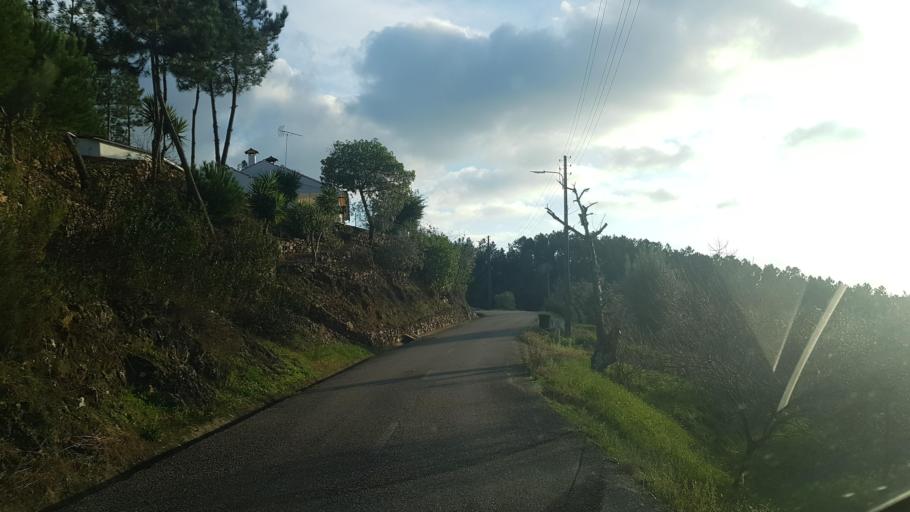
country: PT
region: Castelo Branco
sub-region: Vila de Rei
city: Vila de Rei
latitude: 39.6001
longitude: -8.1205
